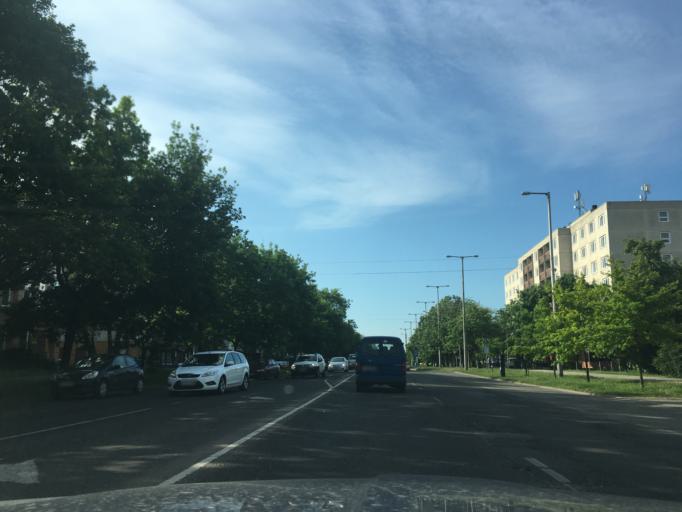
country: HU
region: Hajdu-Bihar
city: Debrecen
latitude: 47.5270
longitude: 21.6321
